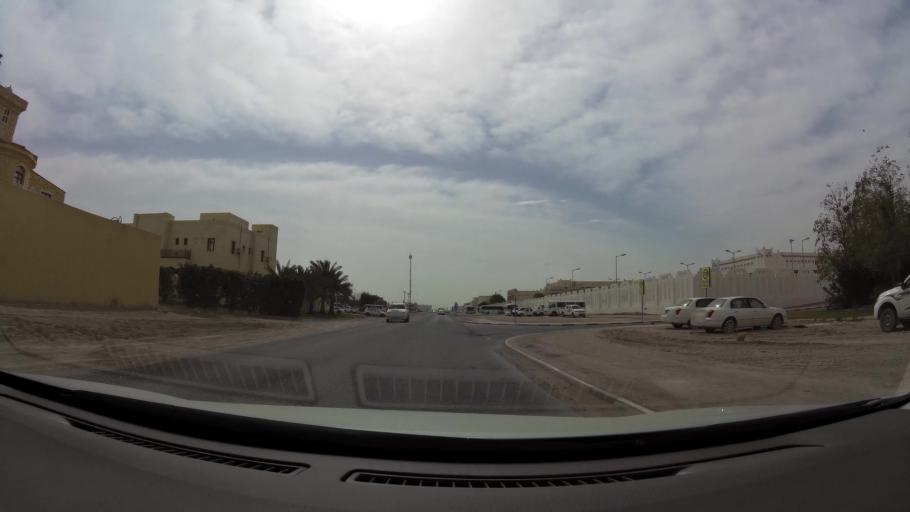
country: QA
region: Baladiyat ad Dawhah
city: Doha
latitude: 25.2238
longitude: 51.4887
